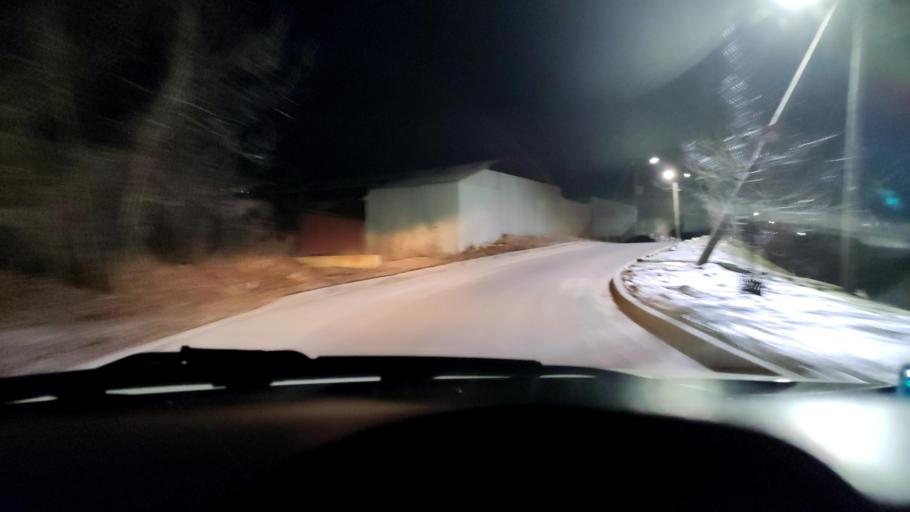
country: RU
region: Voronezj
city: Voronezh
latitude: 51.6328
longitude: 39.1582
